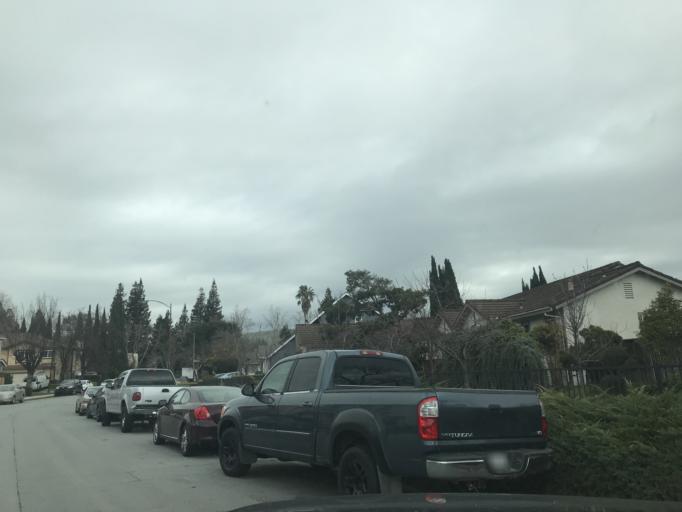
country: US
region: California
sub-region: Santa Clara County
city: Milpitas
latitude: 37.3896
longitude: -121.8744
